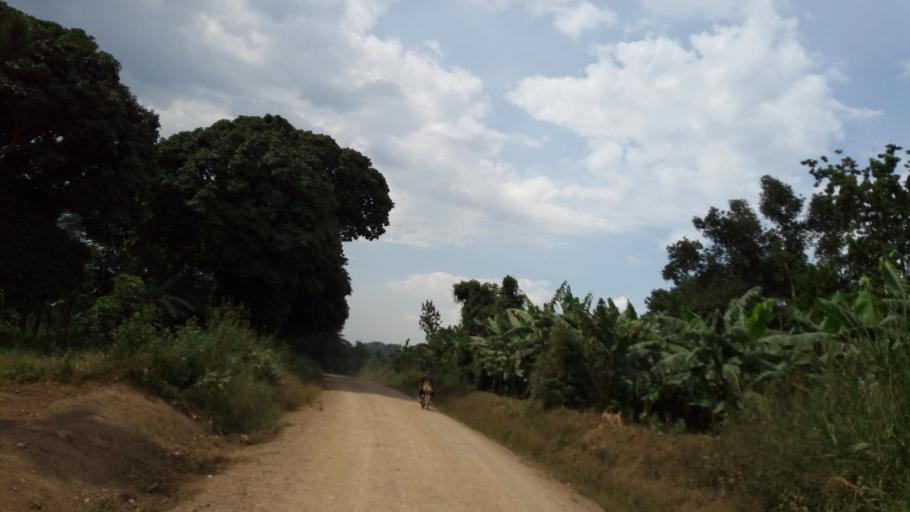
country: UG
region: Central Region
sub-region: Kiboga District
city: Kiboga
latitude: 0.7276
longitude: 31.7339
